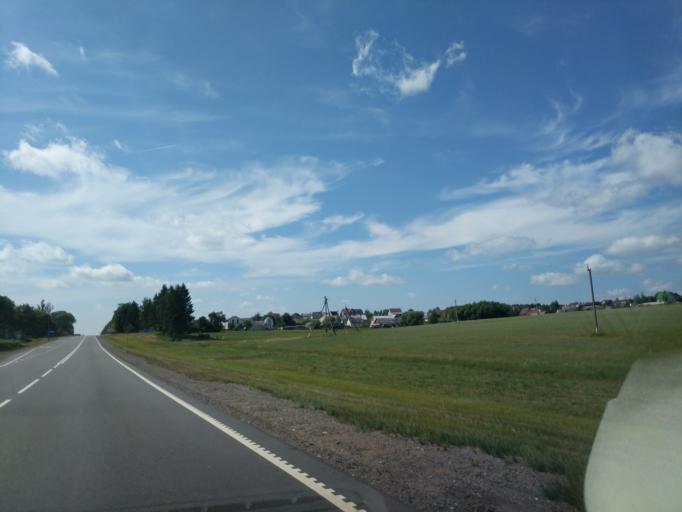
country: BY
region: Minsk
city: Syomkava
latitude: 54.0955
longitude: 27.5068
